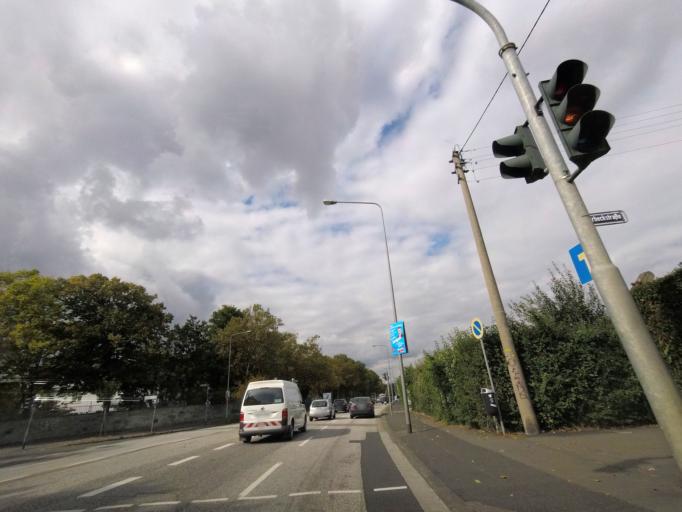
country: DE
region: Hesse
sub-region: Regierungsbezirk Darmstadt
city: Wiesbaden
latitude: 50.0644
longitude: 8.2346
